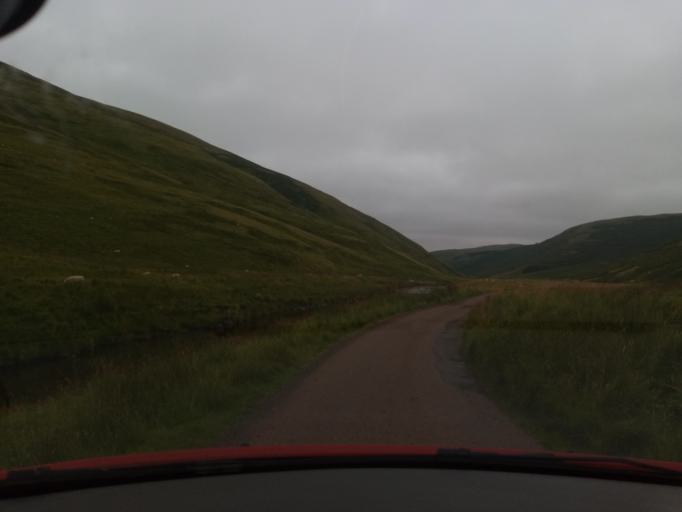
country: GB
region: England
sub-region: Northumberland
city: Rochester
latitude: 55.3849
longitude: -2.2127
